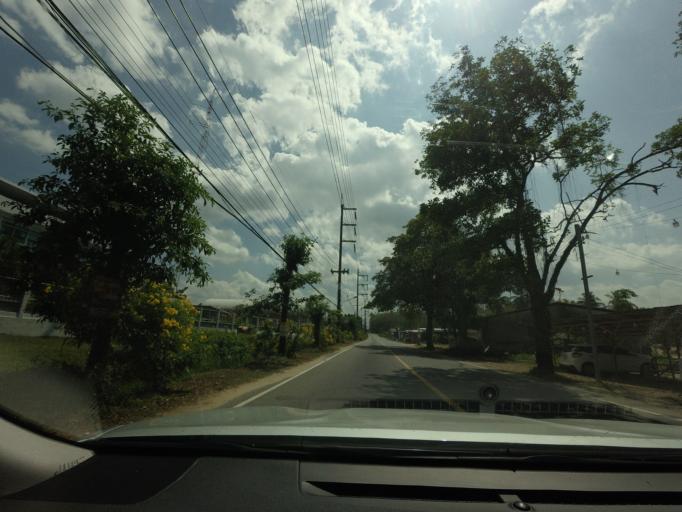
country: TH
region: Phangnga
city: Thai Mueang
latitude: 8.3971
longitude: 98.2608
